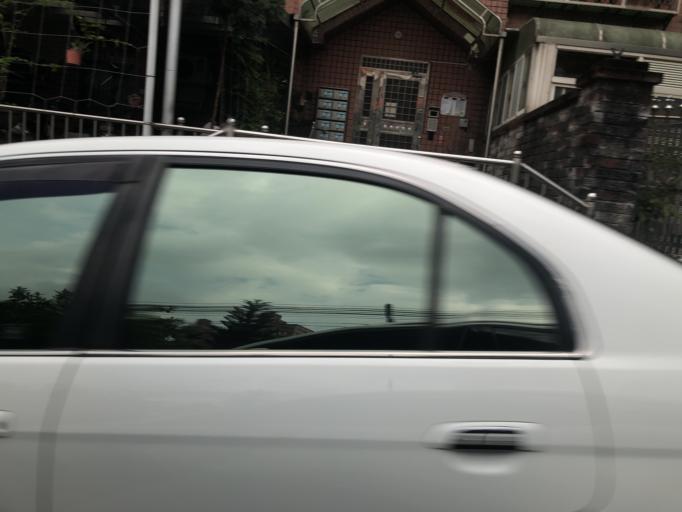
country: TW
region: Taiwan
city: Daxi
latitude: 24.9098
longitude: 121.3567
